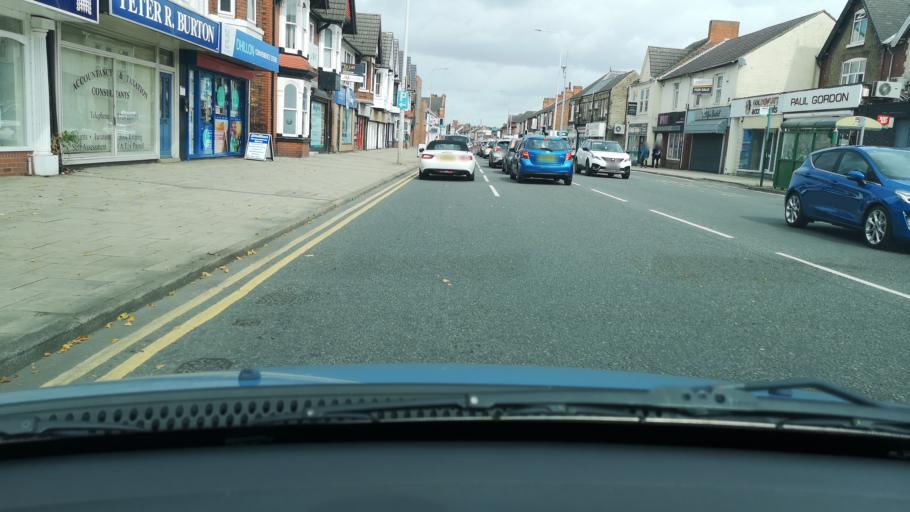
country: GB
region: England
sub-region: North Lincolnshire
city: Scunthorpe
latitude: 53.5891
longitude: -0.6540
